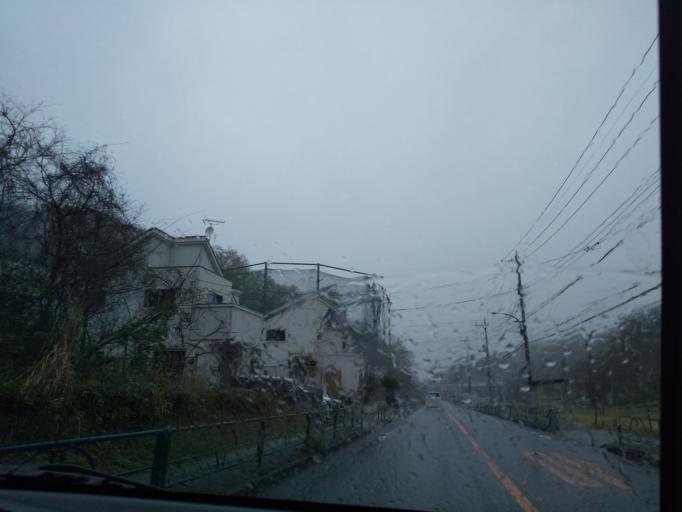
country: JP
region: Tokyo
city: Hino
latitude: 35.6453
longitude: 139.4007
